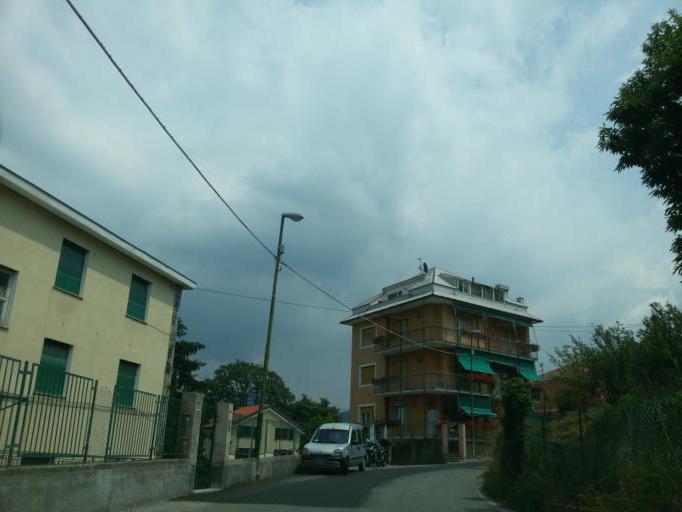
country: IT
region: Liguria
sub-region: Provincia di Genova
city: Piccarello
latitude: 44.4434
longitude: 8.9911
